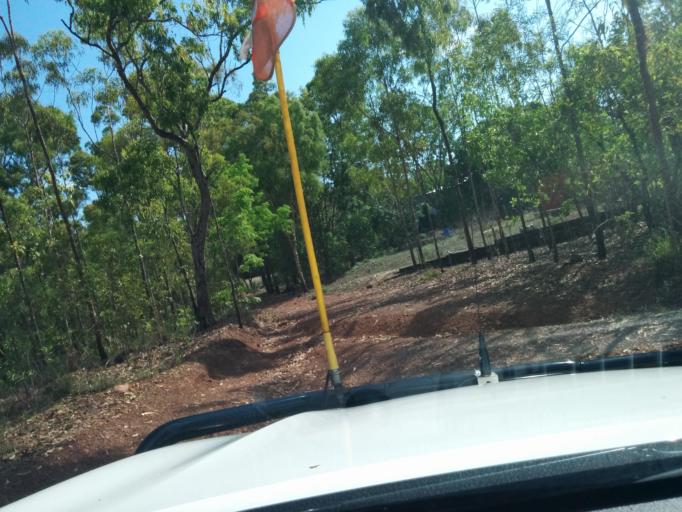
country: AU
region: Northern Territory
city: Alyangula
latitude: -13.8461
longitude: 136.4192
